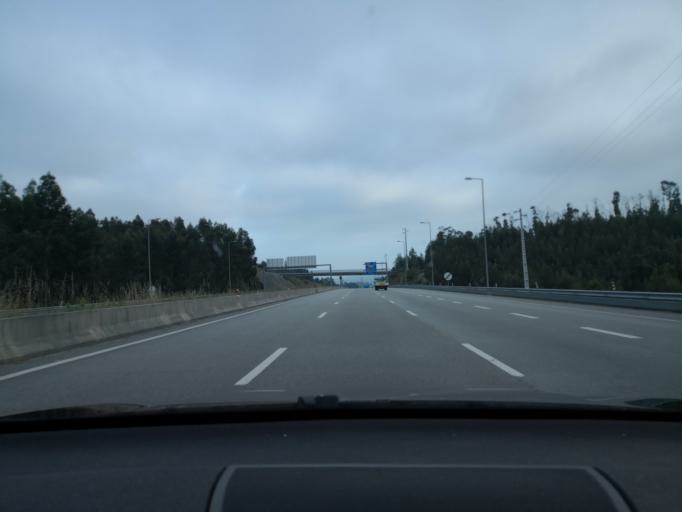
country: PT
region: Porto
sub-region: Gondomar
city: Foz do Sousa
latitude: 41.0913
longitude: -8.4561
